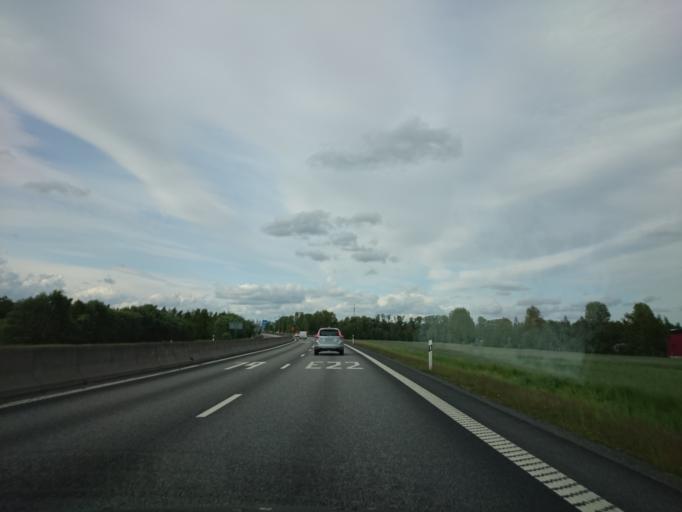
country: SE
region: Skane
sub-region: Kristianstads Kommun
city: Kristianstad
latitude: 56.0126
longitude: 14.1138
